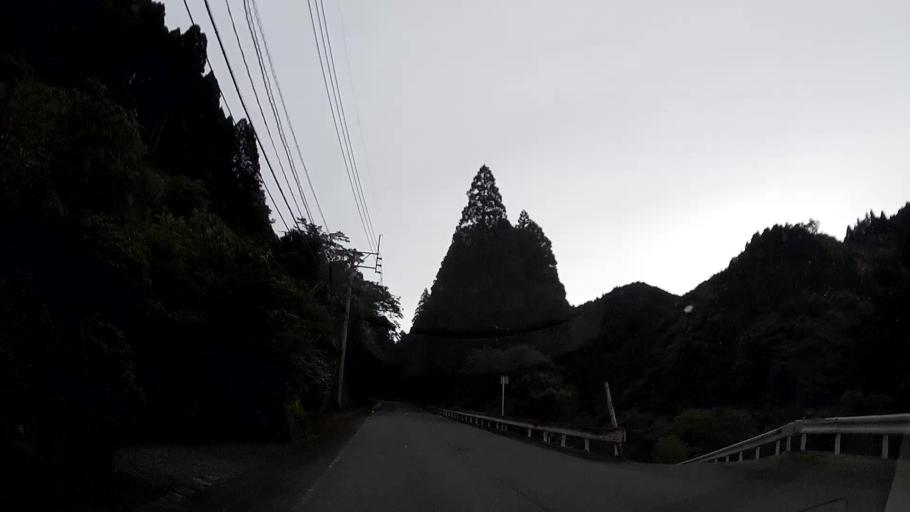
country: JP
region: Kumamoto
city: Kikuchi
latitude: 33.0871
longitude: 130.9522
